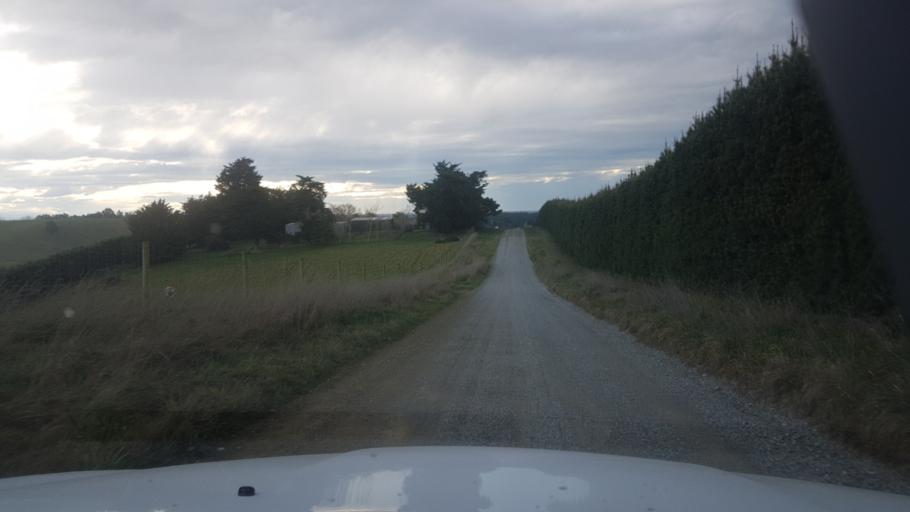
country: NZ
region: Canterbury
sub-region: Timaru District
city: Pleasant Point
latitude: -44.3389
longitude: 171.1463
